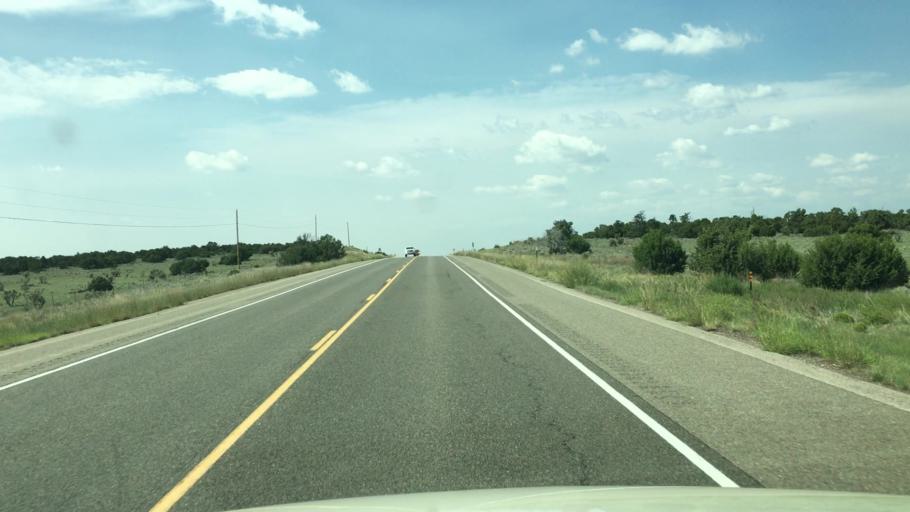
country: US
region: New Mexico
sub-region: Torrance County
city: Moriarty
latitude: 35.0422
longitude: -105.6832
